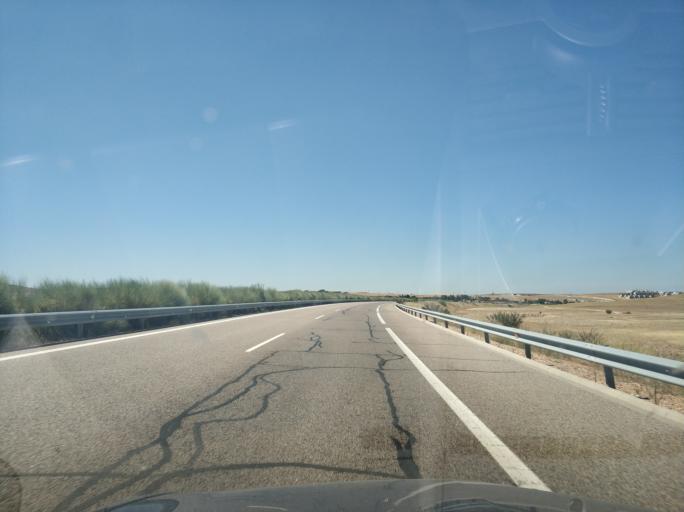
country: ES
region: Castille and Leon
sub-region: Provincia de Salamanca
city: Aldeatejada
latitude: 40.9267
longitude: -5.6750
